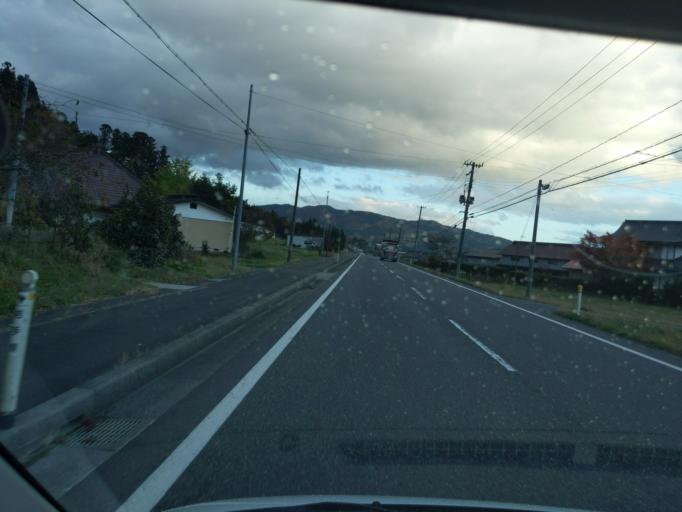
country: JP
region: Iwate
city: Mizusawa
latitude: 39.0457
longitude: 141.1018
